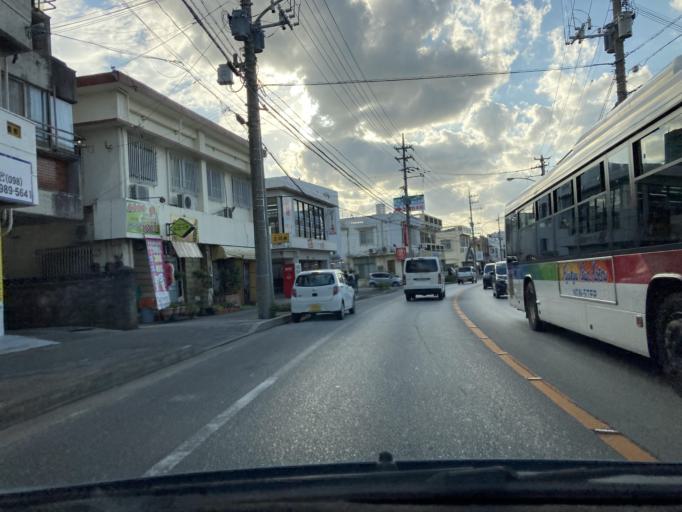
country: JP
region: Okinawa
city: Chatan
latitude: 26.3206
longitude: 127.7865
